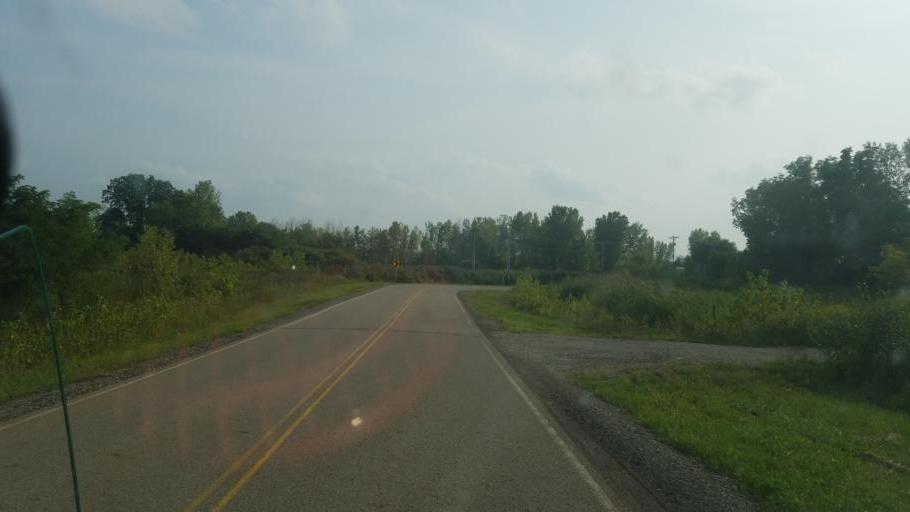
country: US
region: Ohio
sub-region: Medina County
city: Westfield Center
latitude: 41.0076
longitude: -81.9742
